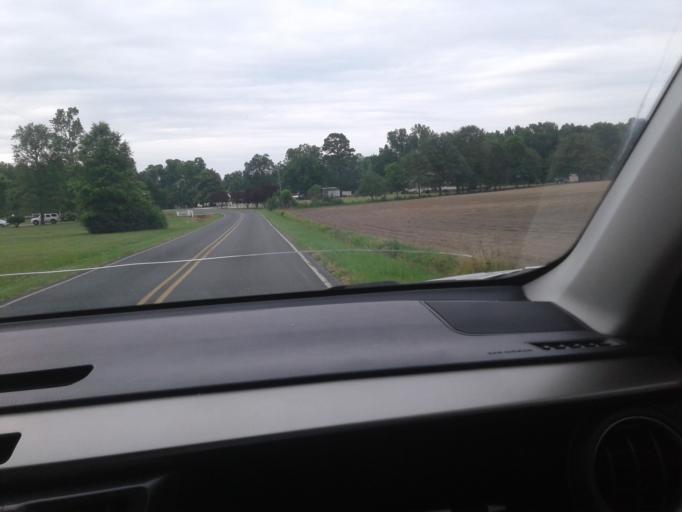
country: US
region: North Carolina
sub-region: Harnett County
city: Dunn
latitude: 35.3380
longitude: -78.5763
